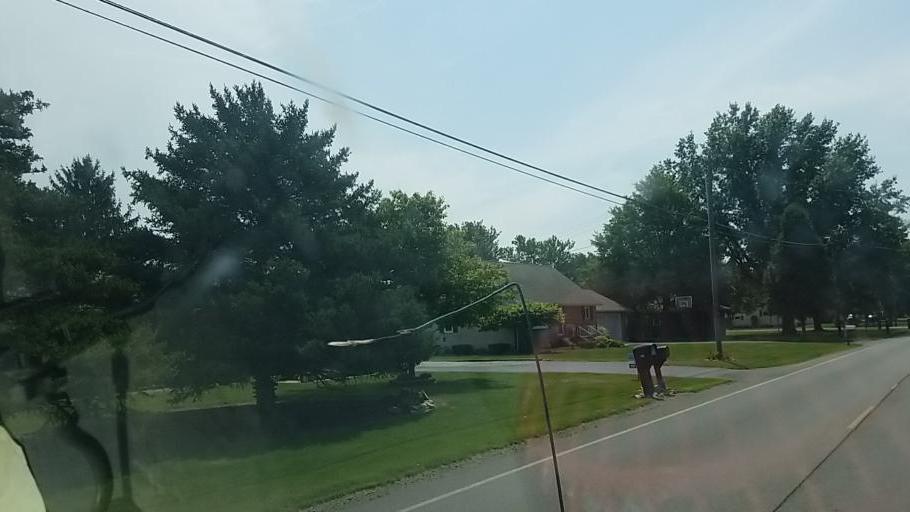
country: US
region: Ohio
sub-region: Marion County
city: Marion
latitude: 40.5865
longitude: -83.0736
